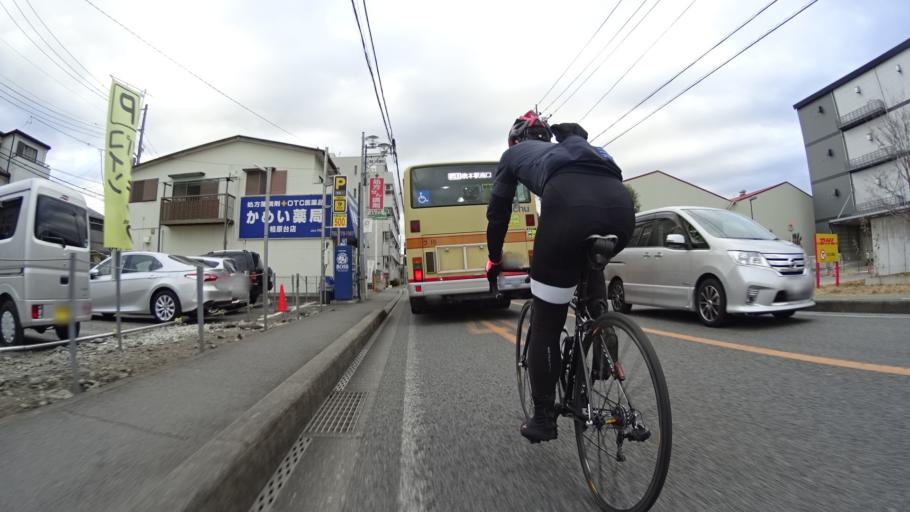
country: JP
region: Tokyo
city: Hachioji
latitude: 35.5986
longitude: 139.3263
